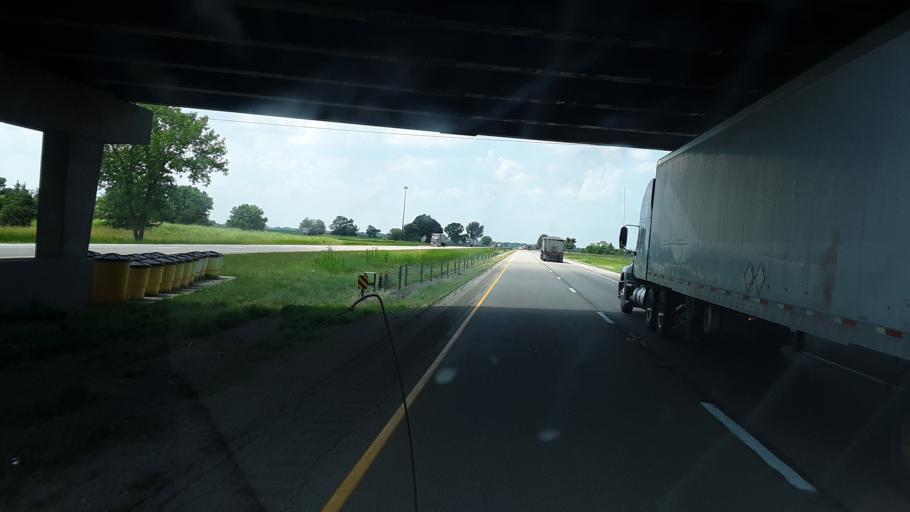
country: US
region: Illinois
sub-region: Bureau County
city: Ladd
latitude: 41.3677
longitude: -89.2184
